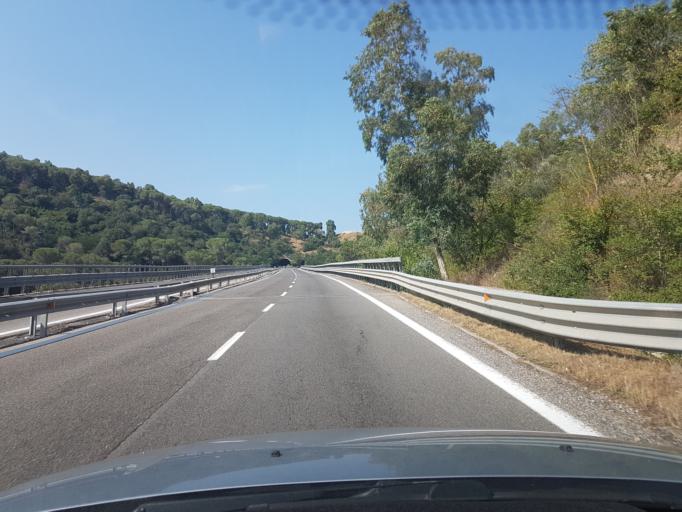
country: IT
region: Sardinia
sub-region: Provincia di Nuoro
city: Nuoro
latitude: 40.3325
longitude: 9.2942
